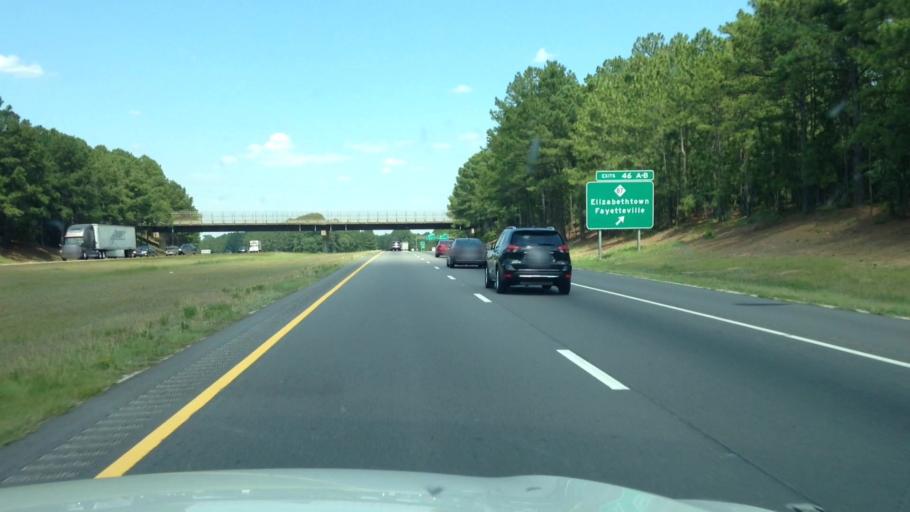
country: US
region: North Carolina
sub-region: Cumberland County
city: Hope Mills
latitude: 34.9719
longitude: -78.8673
